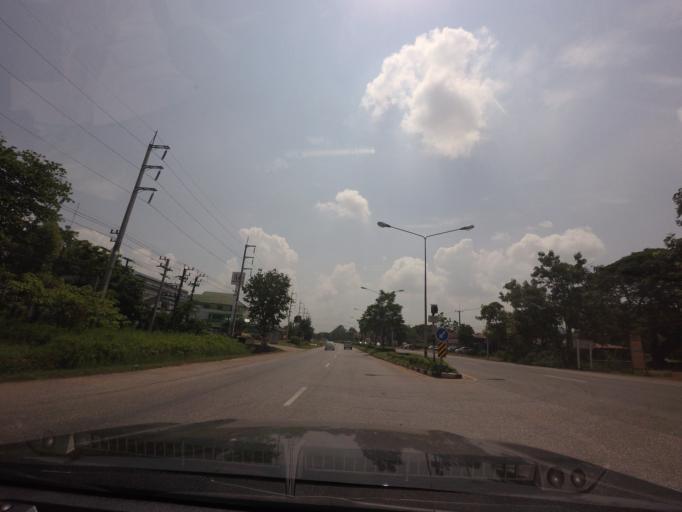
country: TH
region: Uttaradit
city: Uttaradit
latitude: 17.6045
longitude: 100.1236
